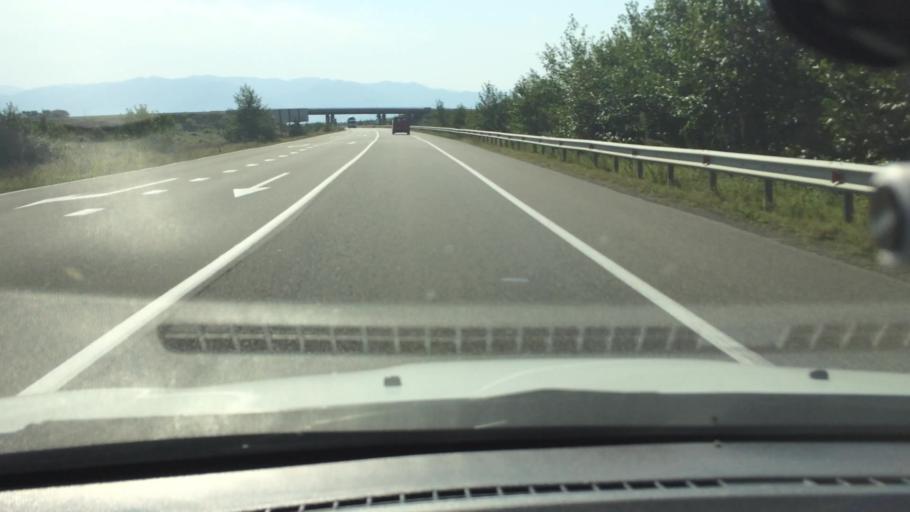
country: GE
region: Guria
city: Urek'i
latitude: 41.9207
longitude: 41.7747
